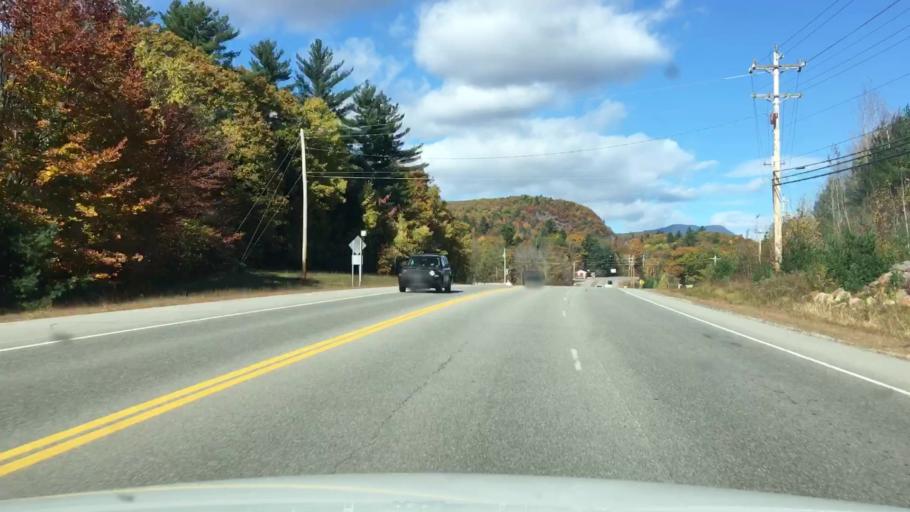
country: US
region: New Hampshire
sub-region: Carroll County
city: North Conway
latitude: 44.1243
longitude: -71.1884
